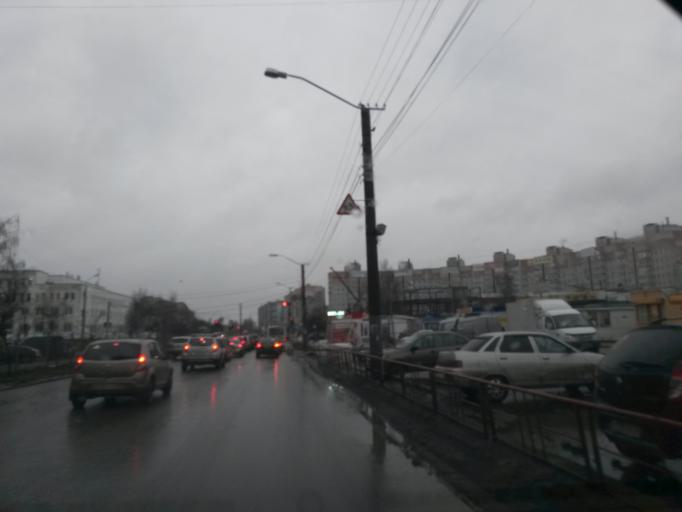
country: RU
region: Jaroslavl
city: Yaroslavl
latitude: 57.6496
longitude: 39.9500
